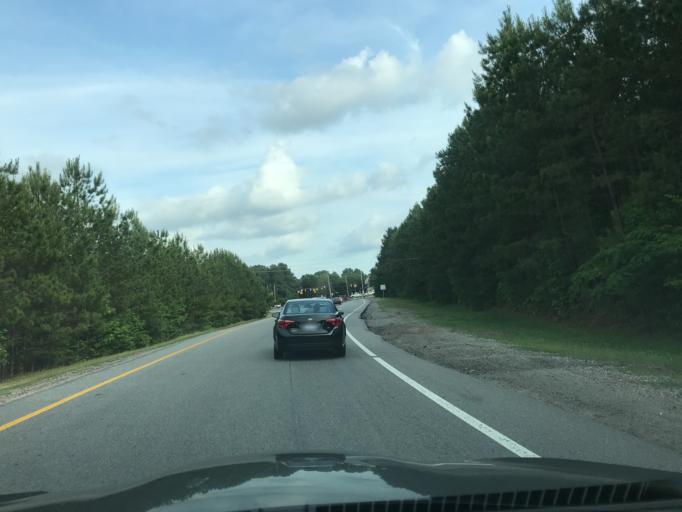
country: US
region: North Carolina
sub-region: Wake County
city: West Raleigh
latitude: 35.8984
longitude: -78.6129
